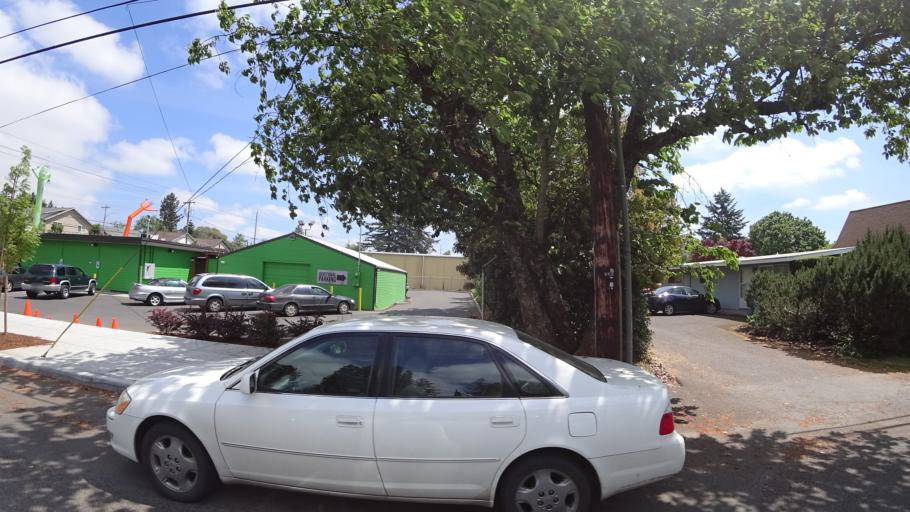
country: US
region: Oregon
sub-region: Multnomah County
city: Gresham
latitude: 45.5040
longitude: -122.4874
